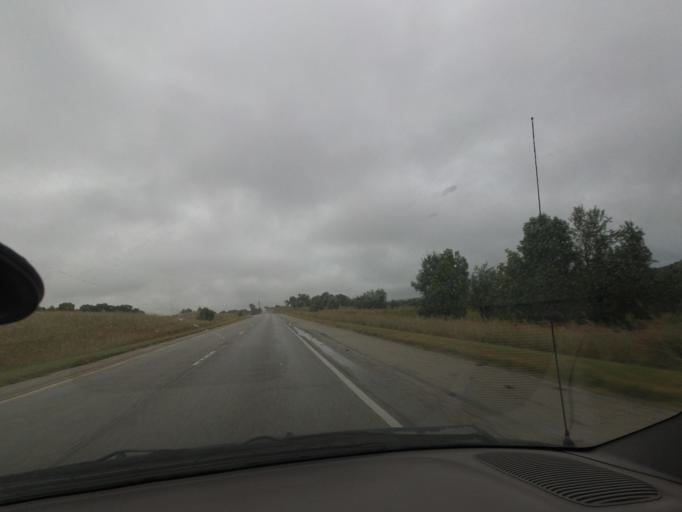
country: US
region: Illinois
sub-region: Pike County
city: Barry
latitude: 39.7317
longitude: -91.1239
